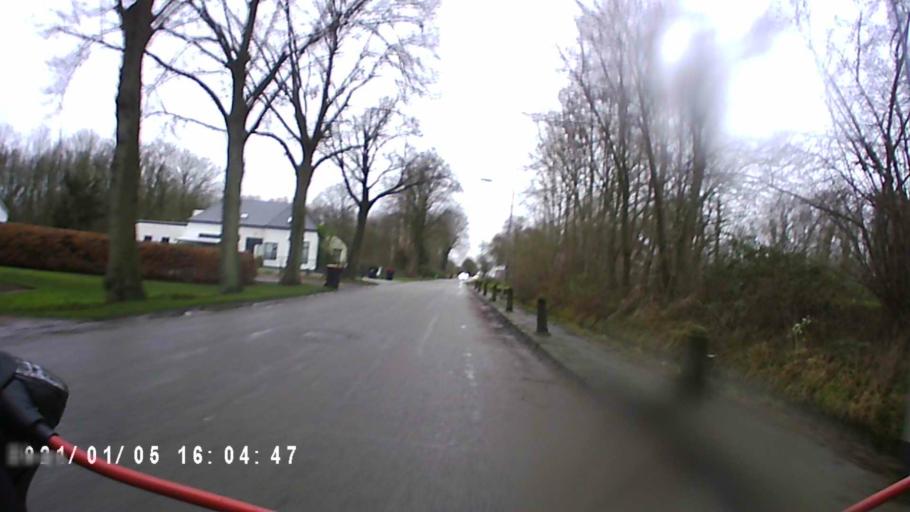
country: NL
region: Groningen
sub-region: Gemeente  Oldambt
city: Winschoten
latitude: 53.1989
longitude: 7.0808
